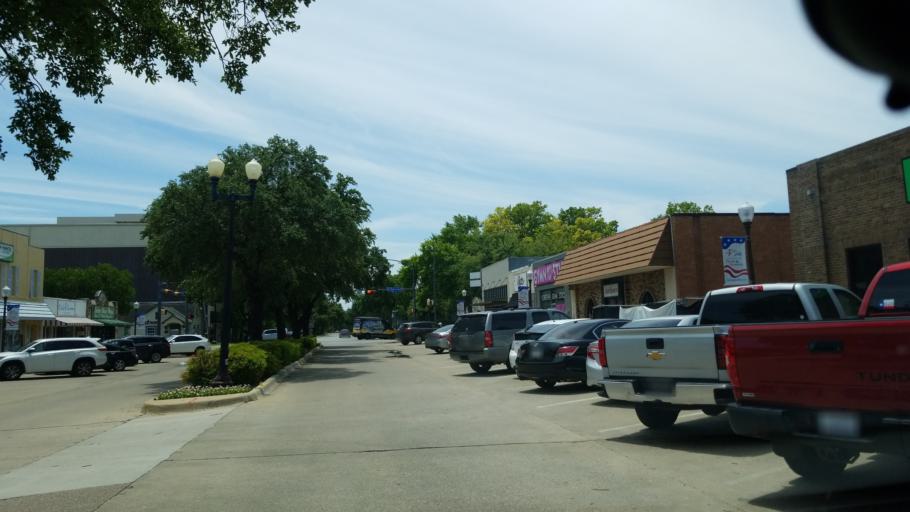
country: US
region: Texas
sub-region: Dallas County
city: Irving
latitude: 32.8135
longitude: -96.9462
